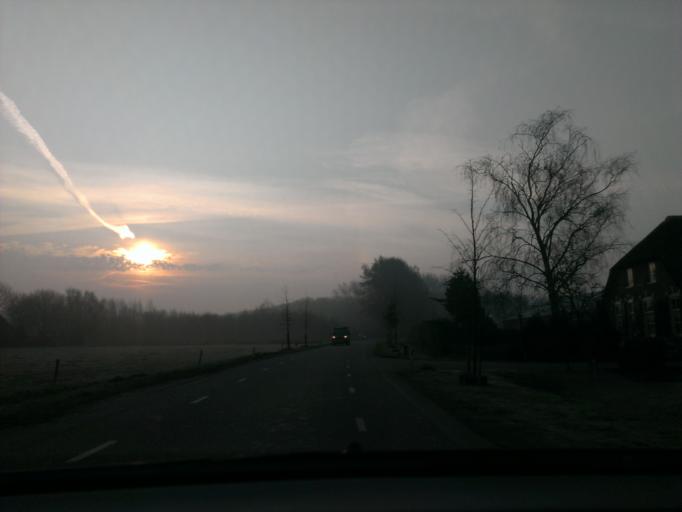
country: NL
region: Gelderland
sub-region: Gemeente Voorst
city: Twello
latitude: 52.2280
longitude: 6.0569
